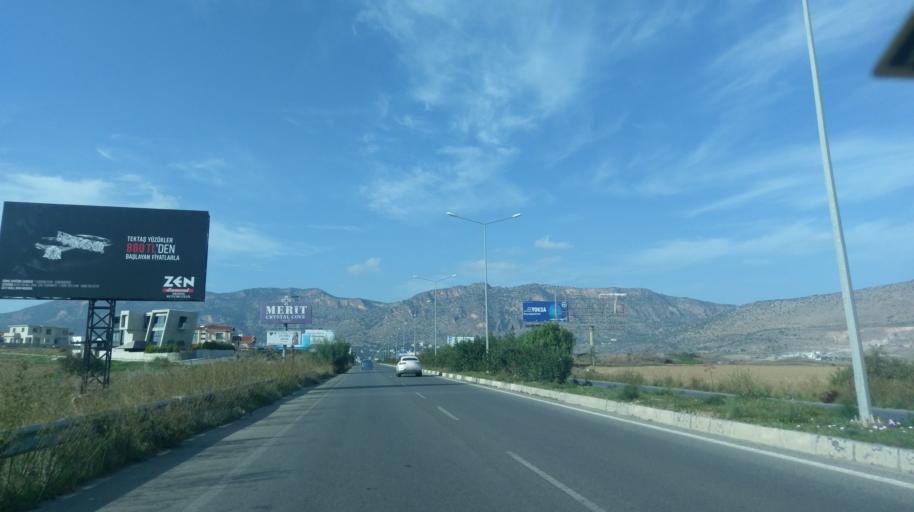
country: CY
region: Keryneia
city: Kyrenia
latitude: 35.2681
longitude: 33.2914
